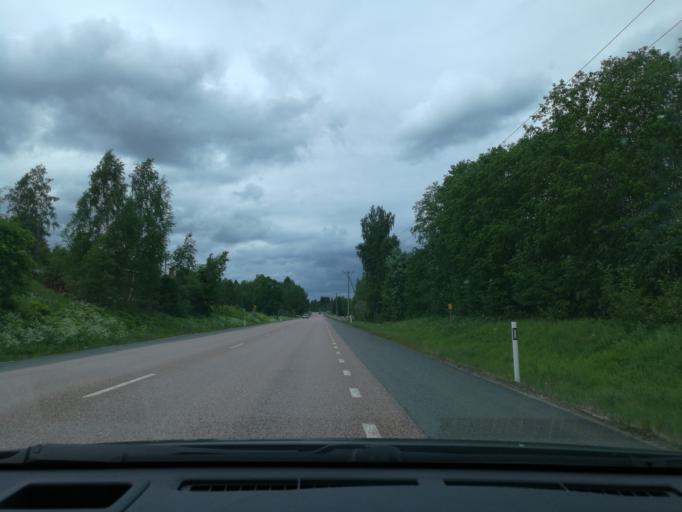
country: SE
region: Vaestmanland
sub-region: Fagersta Kommun
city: Fagersta
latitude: 59.9920
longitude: 15.6713
